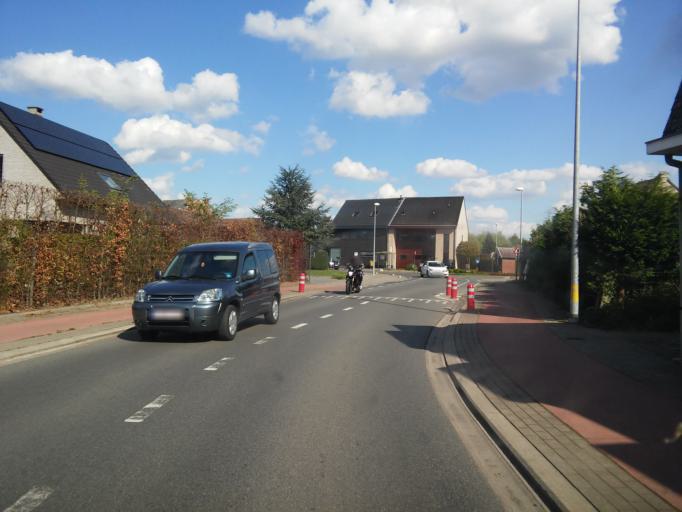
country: BE
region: Flanders
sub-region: Provincie Antwerpen
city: Puurs
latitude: 51.0815
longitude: 4.3198
